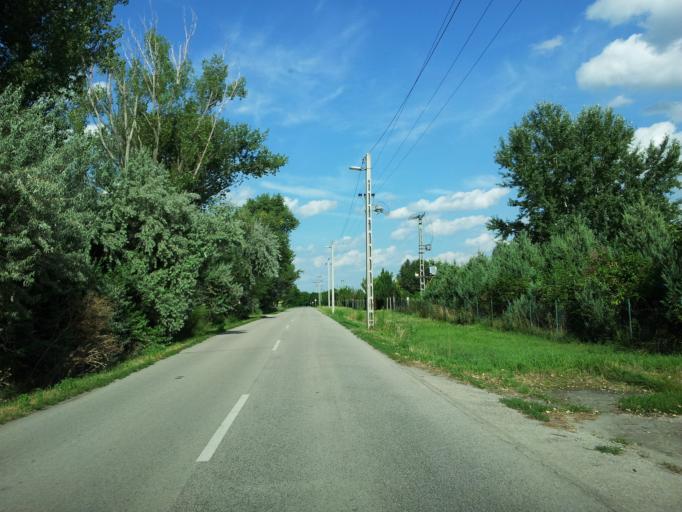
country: HU
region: Pest
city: Szigetcsep
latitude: 47.2626
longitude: 19.0031
